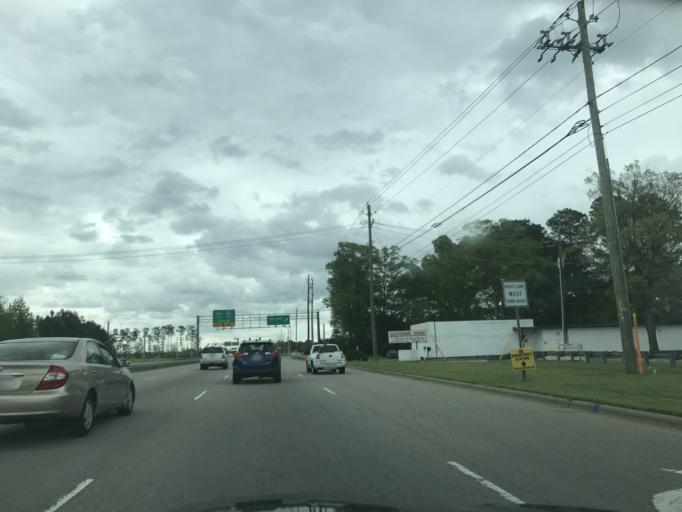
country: US
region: North Carolina
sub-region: Wake County
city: Knightdale
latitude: 35.7952
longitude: -78.5192
